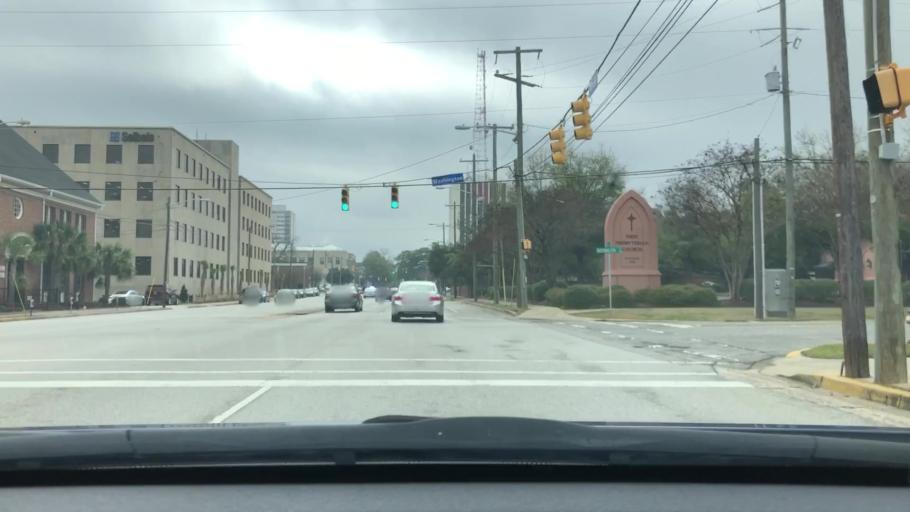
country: US
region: South Carolina
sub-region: Richland County
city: Columbia
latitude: 34.0056
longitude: -81.0301
